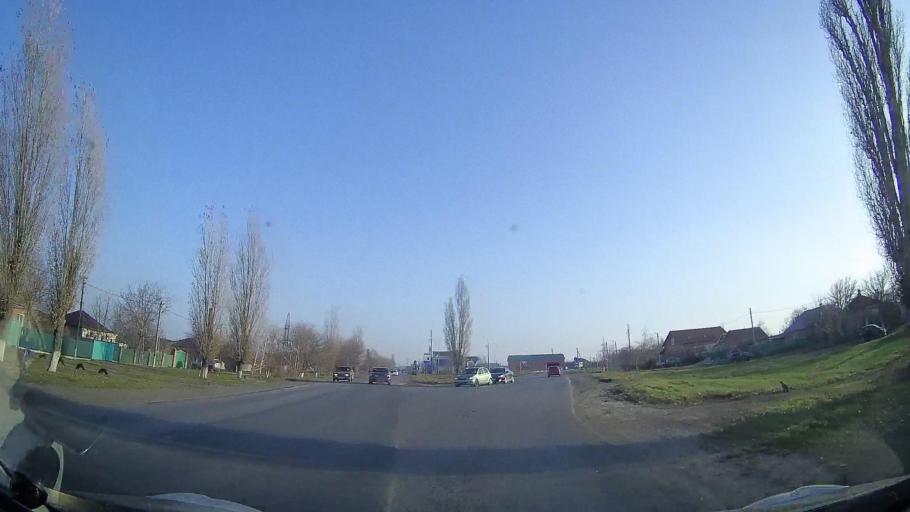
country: RU
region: Rostov
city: Ol'ginskaya
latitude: 47.1833
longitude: 39.9574
